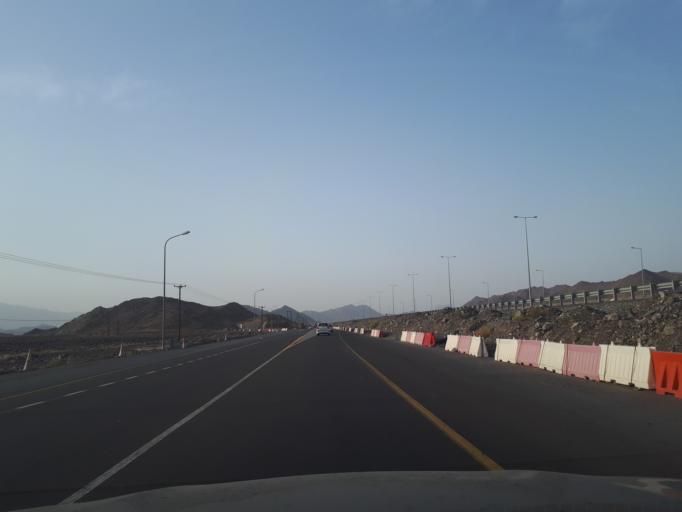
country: OM
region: Muhafazat ad Dakhiliyah
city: Sufalat Sama'il
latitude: 23.2812
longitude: 58.1075
